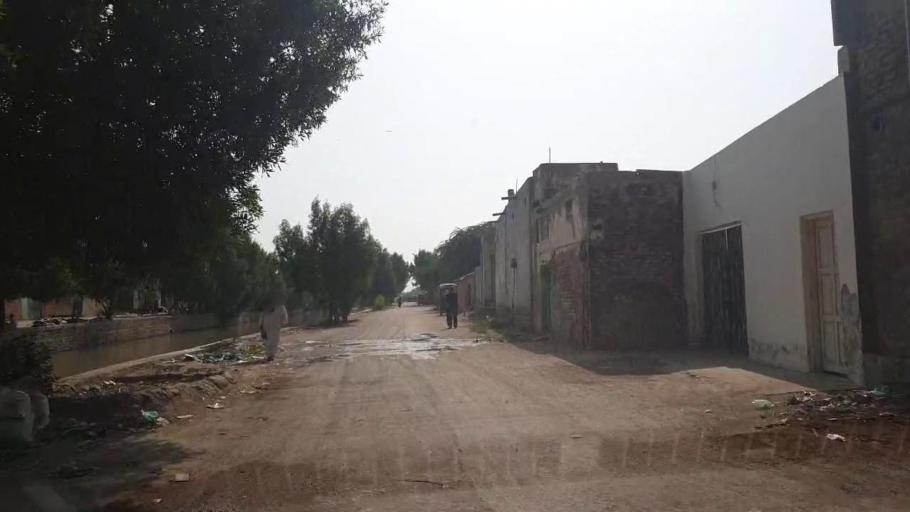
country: PK
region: Sindh
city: Badin
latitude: 24.6560
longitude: 68.8413
